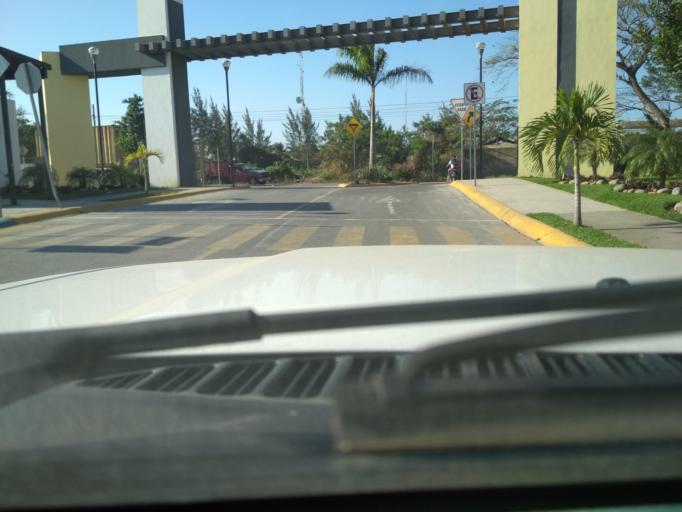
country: MX
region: Veracruz
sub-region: Veracruz
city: Las Amapolas
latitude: 19.1473
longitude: -96.2354
